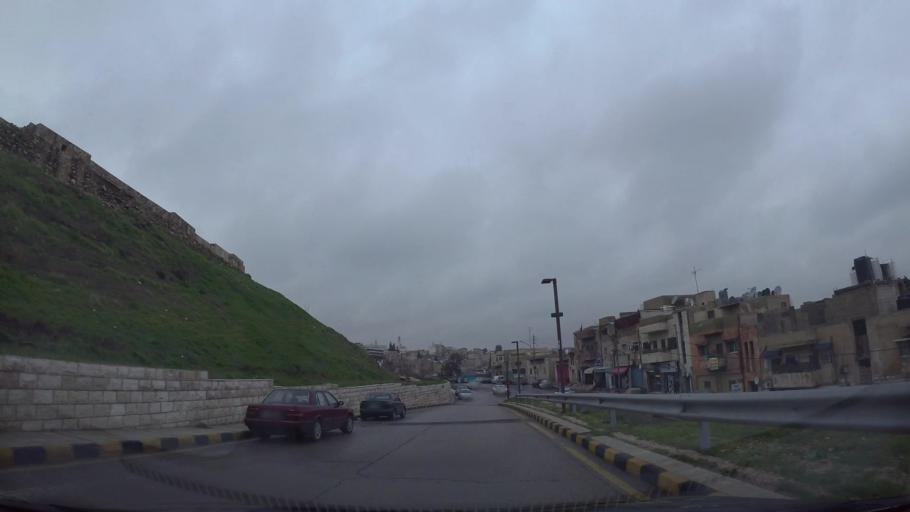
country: JO
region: Amman
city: Amman
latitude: 31.9555
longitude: 35.9356
